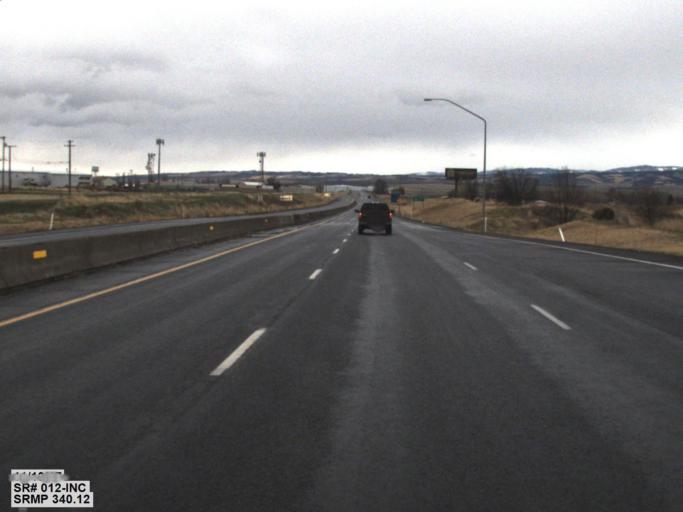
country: US
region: Washington
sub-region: Walla Walla County
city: Walla Walla East
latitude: 46.0845
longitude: -118.2762
